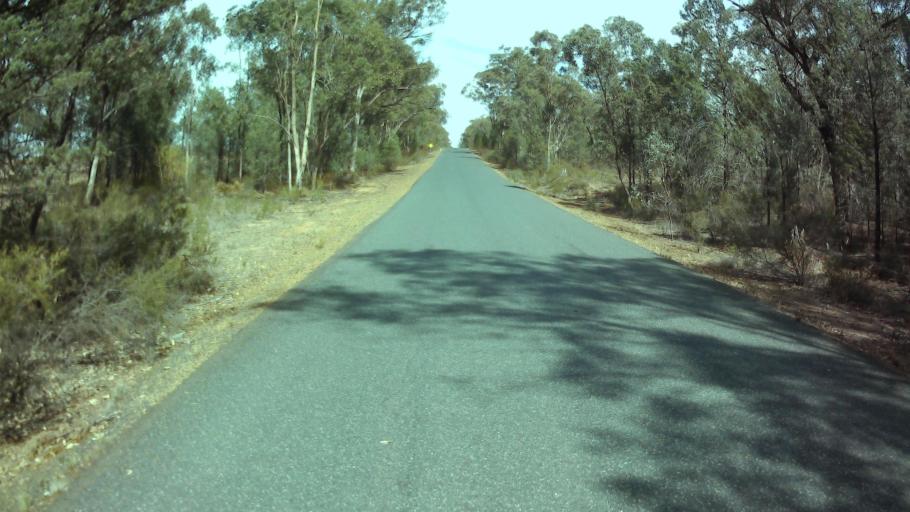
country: AU
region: New South Wales
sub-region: Weddin
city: Grenfell
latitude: -33.8069
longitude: 148.0508
